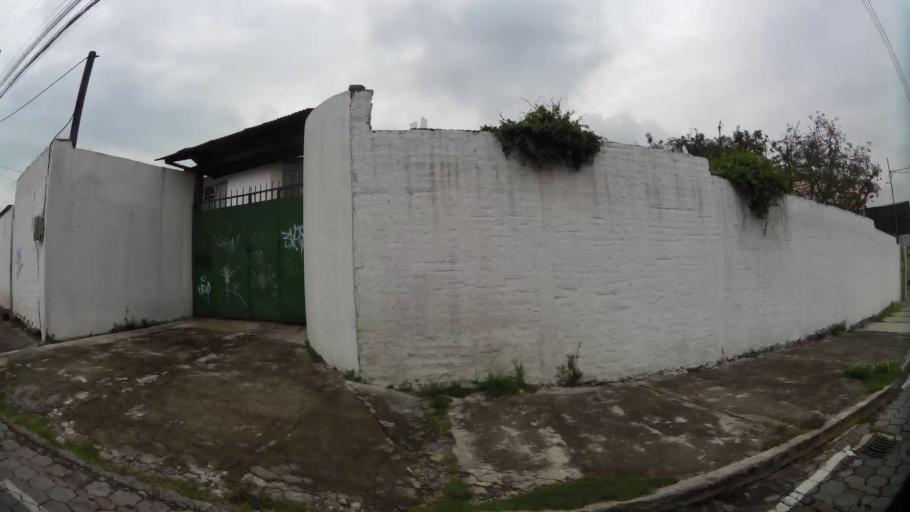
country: EC
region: Pichincha
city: Sangolqui
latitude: -0.3079
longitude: -78.4561
